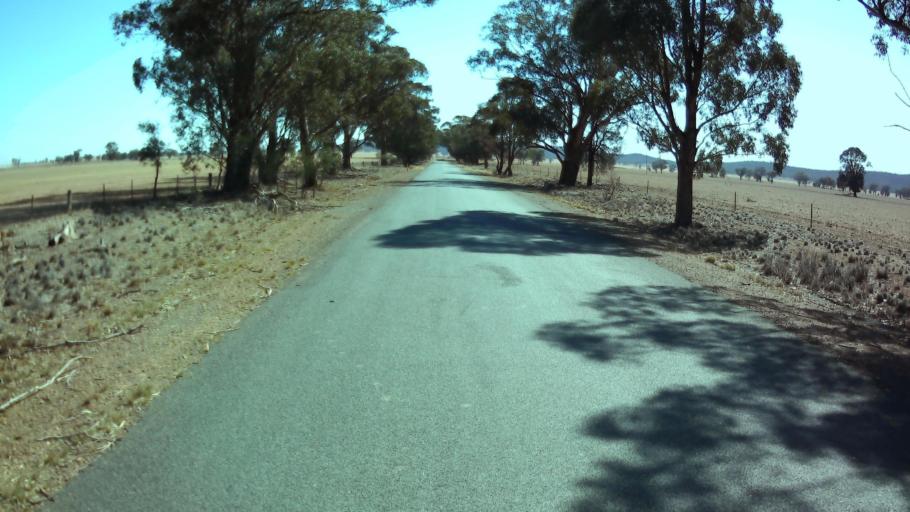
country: AU
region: New South Wales
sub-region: Weddin
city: Grenfell
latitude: -33.7086
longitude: 147.9142
